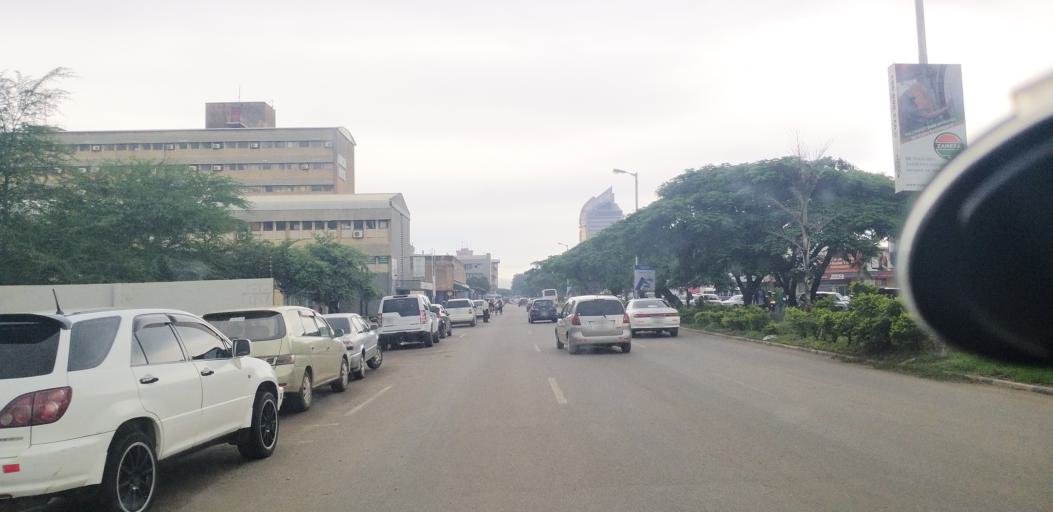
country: ZM
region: Lusaka
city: Lusaka
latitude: -15.4122
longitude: 28.2811
